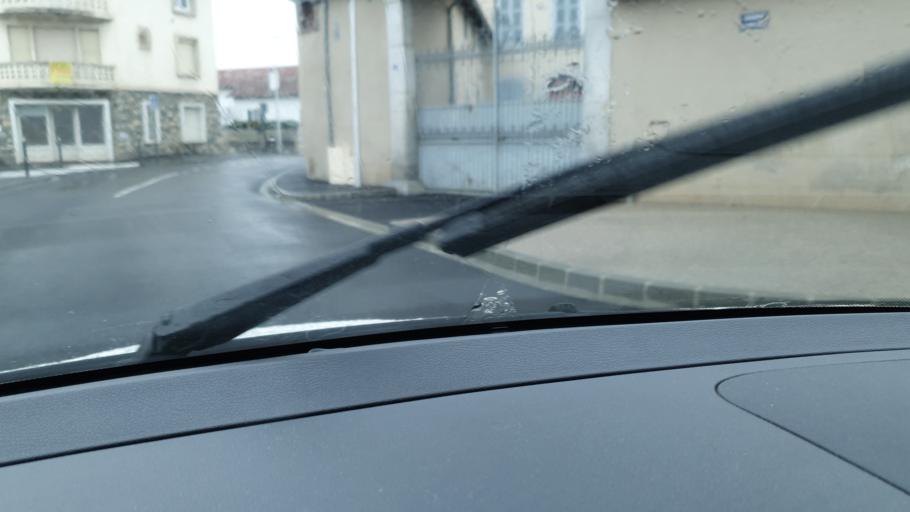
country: FR
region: Midi-Pyrenees
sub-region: Departement des Hautes-Pyrenees
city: Oursbelille
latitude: 43.2547
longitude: 0.0522
